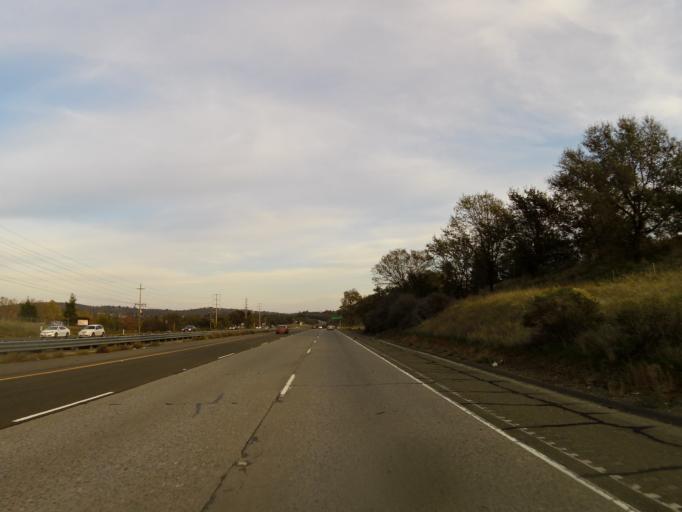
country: US
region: California
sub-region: El Dorado County
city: Cameron Park
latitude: 38.6556
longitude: -121.0073
